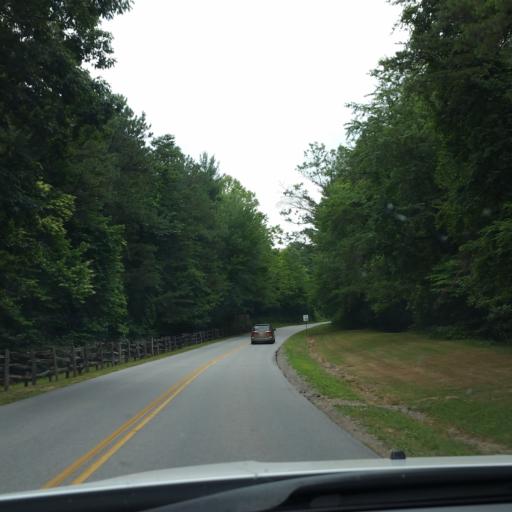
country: US
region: North Carolina
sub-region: Buncombe County
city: Biltmore Forest
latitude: 35.5628
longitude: -82.4923
